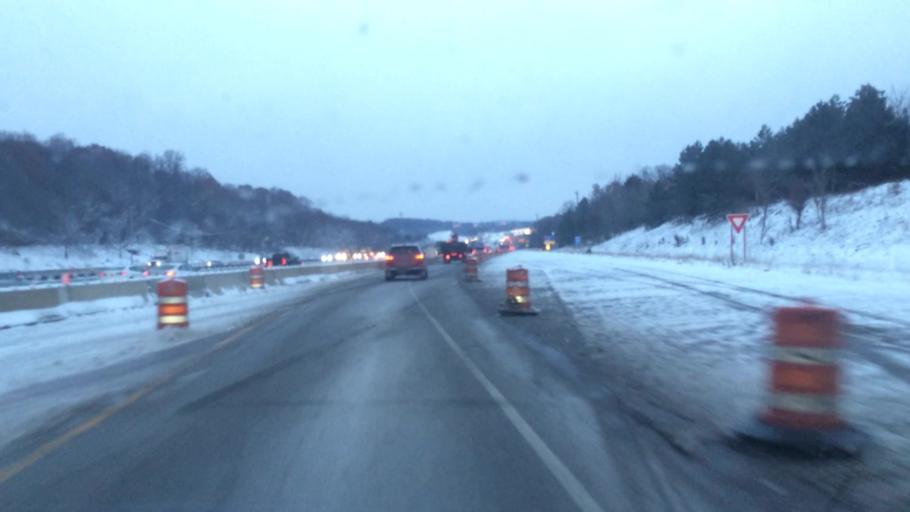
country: US
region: Ohio
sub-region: Cuyahoga County
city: Oakwood
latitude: 41.3767
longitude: -81.5131
